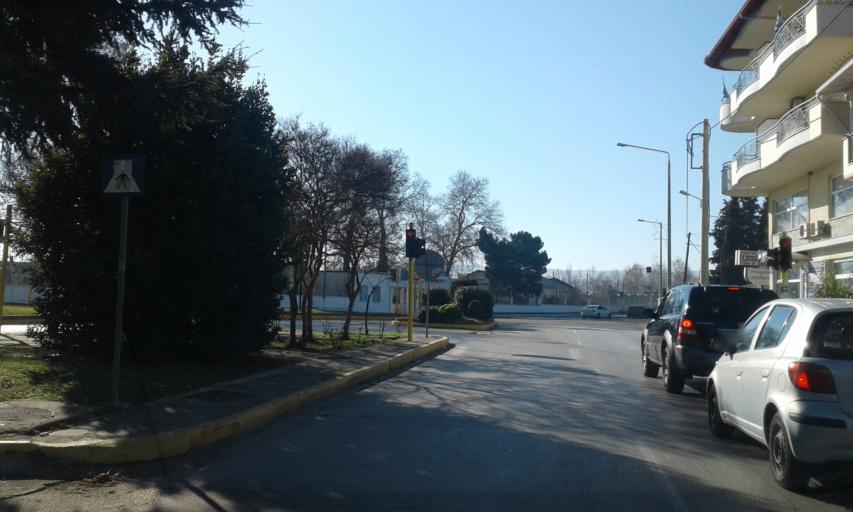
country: GR
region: Central Macedonia
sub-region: Nomos Thessalonikis
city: Lagkadas
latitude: 40.7475
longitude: 23.0620
